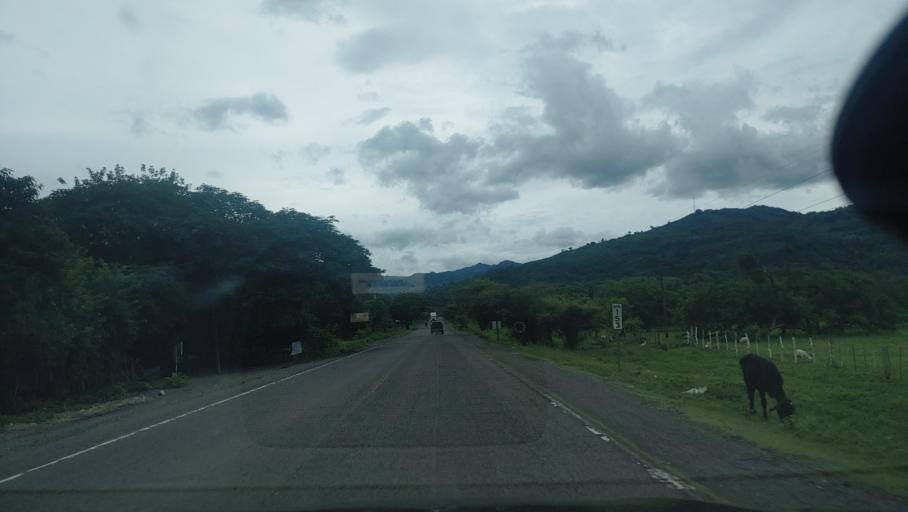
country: HN
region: Choluteca
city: Santa Ana de Yusguare
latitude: 13.3617
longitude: -87.0897
